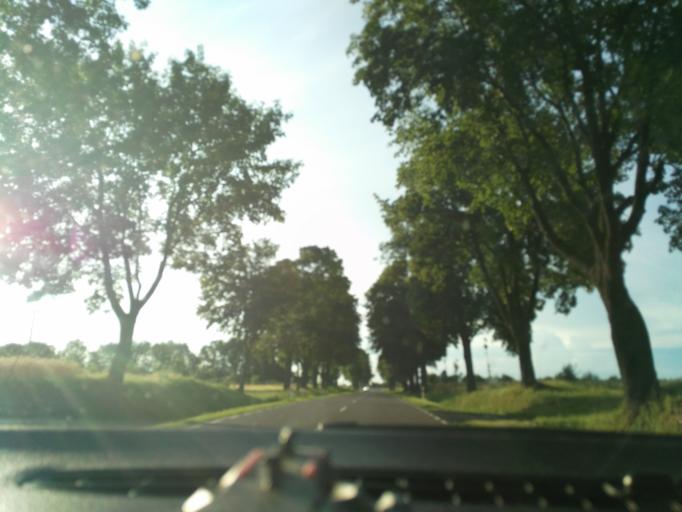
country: PL
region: Lublin Voivodeship
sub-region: Powiat krasnicki
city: Krasnik
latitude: 50.8781
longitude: 22.2645
